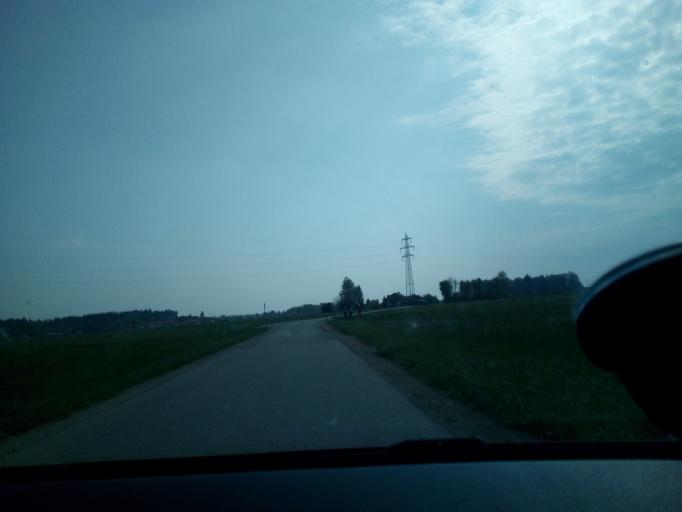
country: DE
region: Bavaria
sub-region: Upper Bavaria
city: Otterfing
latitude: 47.8834
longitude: 11.6730
